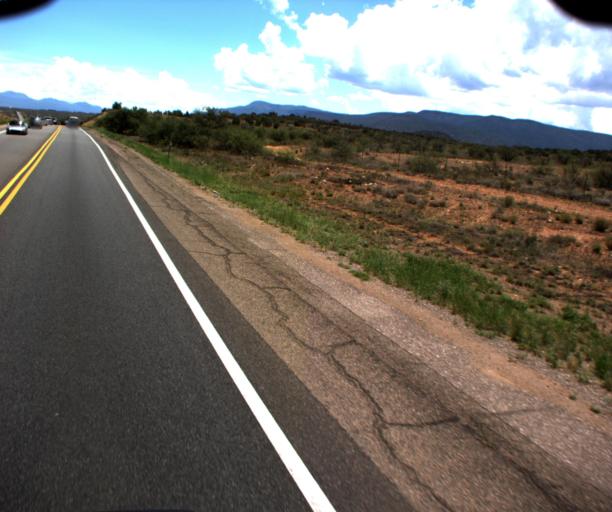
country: US
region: Arizona
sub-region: Yavapai County
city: Cornville
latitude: 34.6500
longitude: -111.9563
